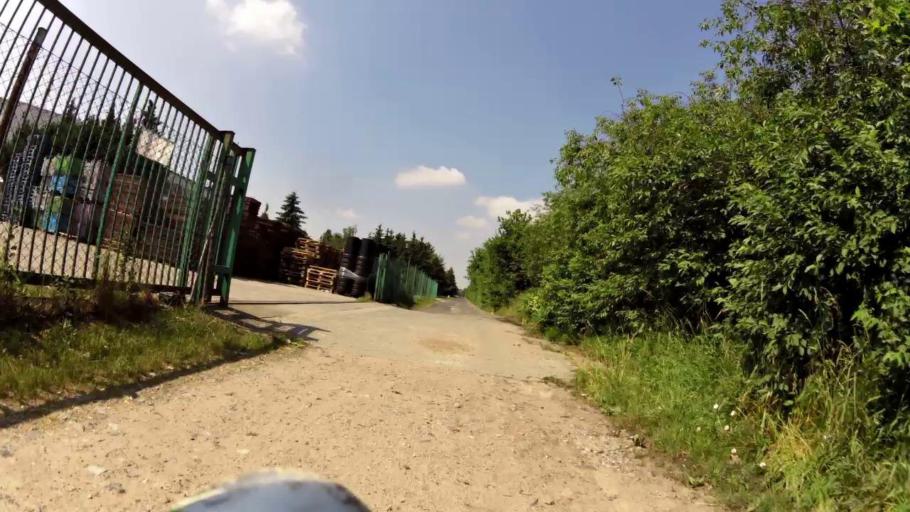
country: PL
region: Kujawsko-Pomorskie
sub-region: Powiat bydgoski
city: Koronowo
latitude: 53.2845
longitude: 17.9384
